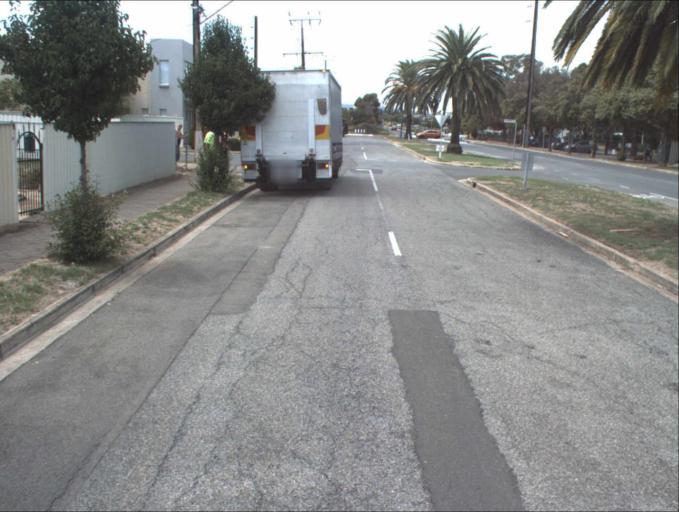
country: AU
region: South Australia
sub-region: Port Adelaide Enfield
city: Klemzig
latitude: -34.8582
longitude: 138.6255
